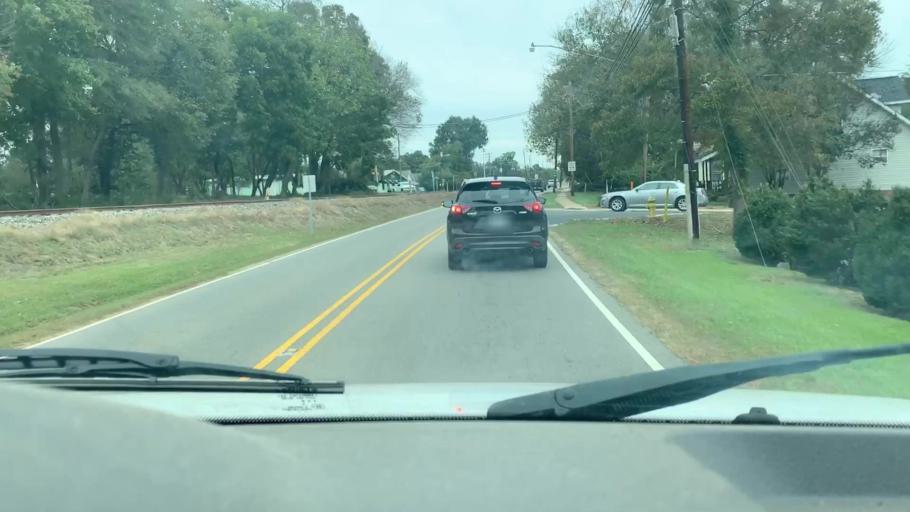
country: US
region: North Carolina
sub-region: Iredell County
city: Mooresville
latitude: 35.5716
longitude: -80.8259
